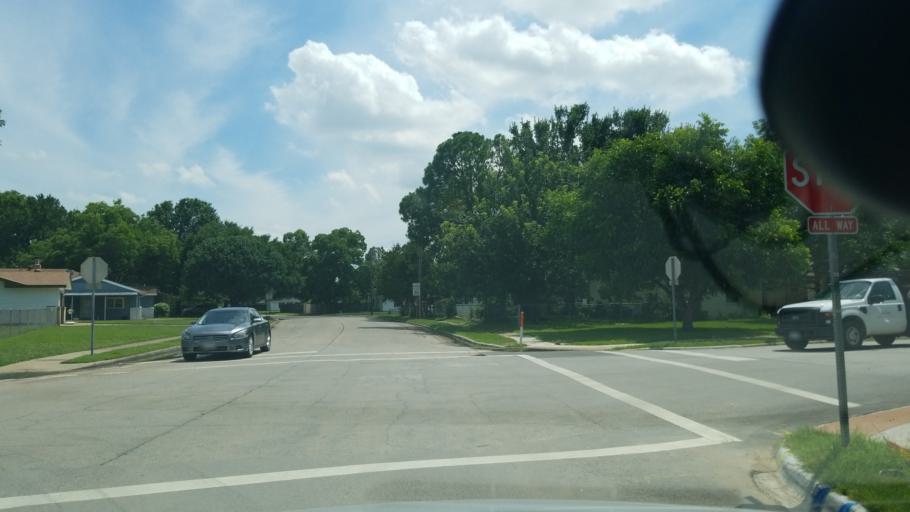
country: US
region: Texas
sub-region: Dallas County
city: Irving
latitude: 32.8513
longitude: -96.9680
